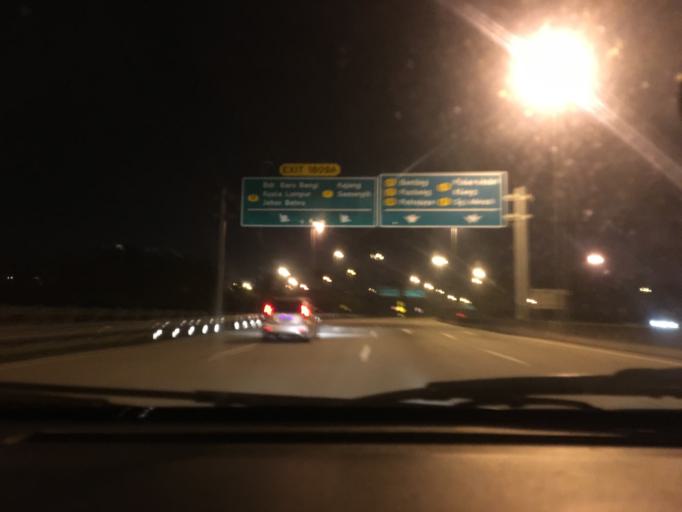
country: MY
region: Selangor
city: Kampong Baharu Balakong
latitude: 2.9845
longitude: 101.7314
